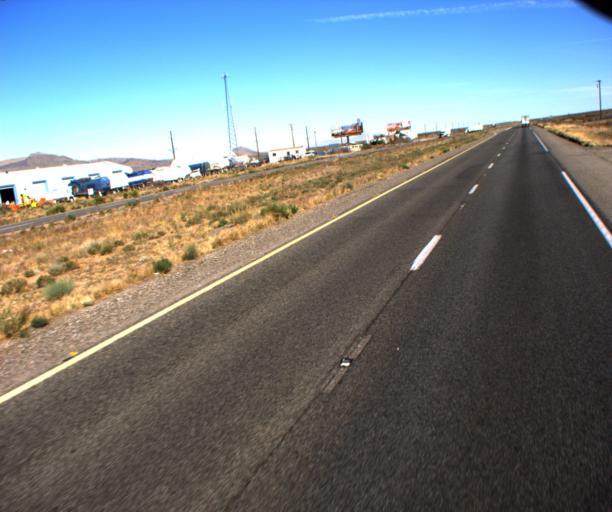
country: US
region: Arizona
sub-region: Mohave County
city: Golden Valley
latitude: 35.3340
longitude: -114.2137
